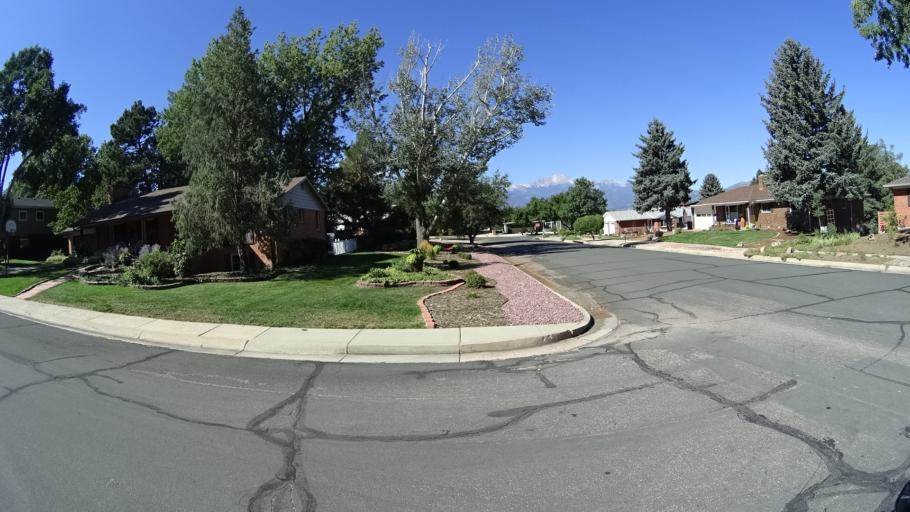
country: US
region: Colorado
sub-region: El Paso County
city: Colorado Springs
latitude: 38.8752
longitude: -104.7852
